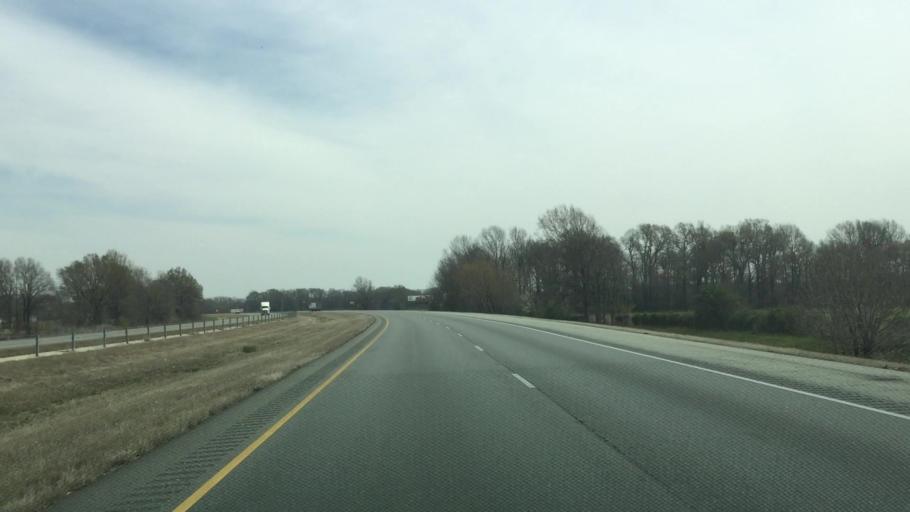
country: US
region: Arkansas
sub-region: Saint Francis County
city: Forrest City
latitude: 34.9767
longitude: -90.9238
